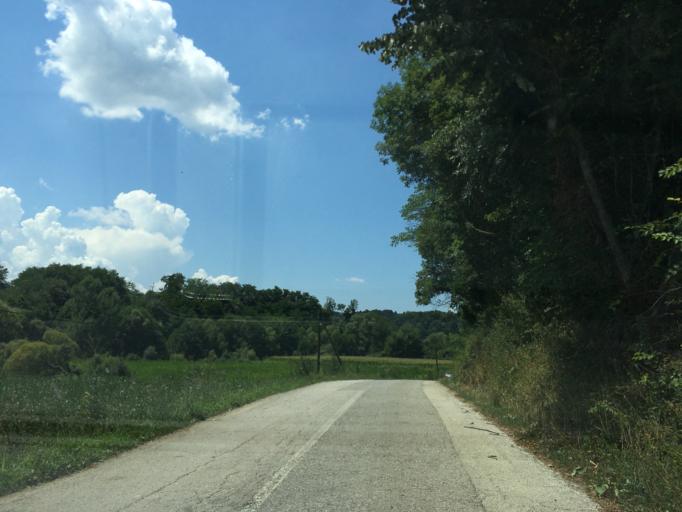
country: RS
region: Central Serbia
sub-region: Kolubarski Okrug
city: Ljig
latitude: 44.2398
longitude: 20.3675
